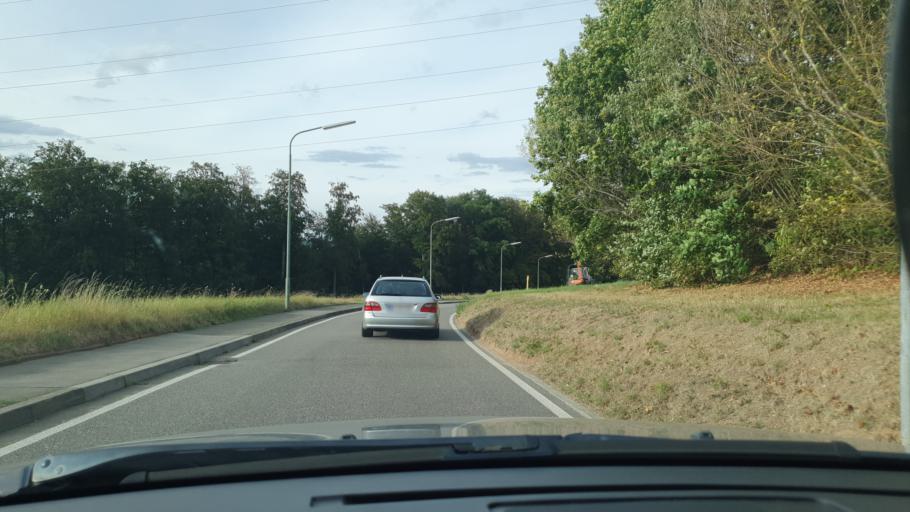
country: DE
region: Rheinland-Pfalz
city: Otterbach
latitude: 49.4753
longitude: 7.7658
